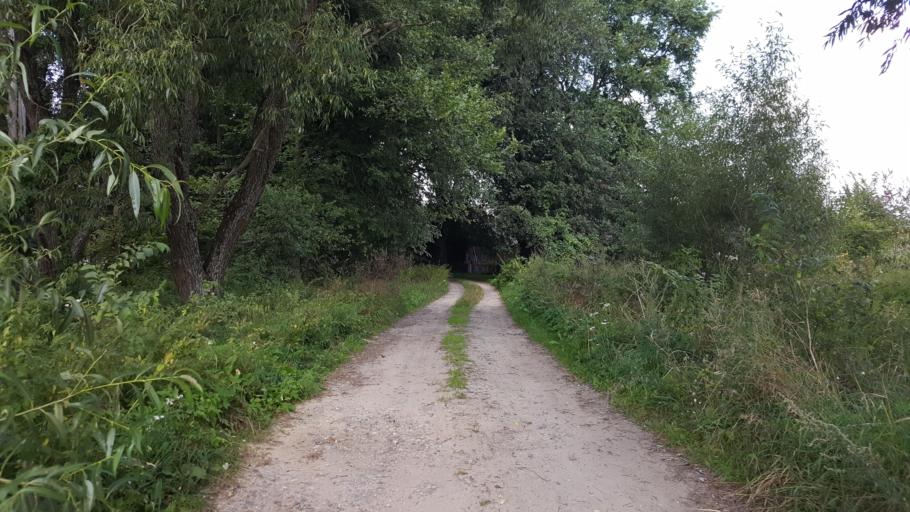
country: PL
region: Podlasie
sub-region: Powiat hajnowski
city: Hajnowka
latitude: 52.5654
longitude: 23.6118
